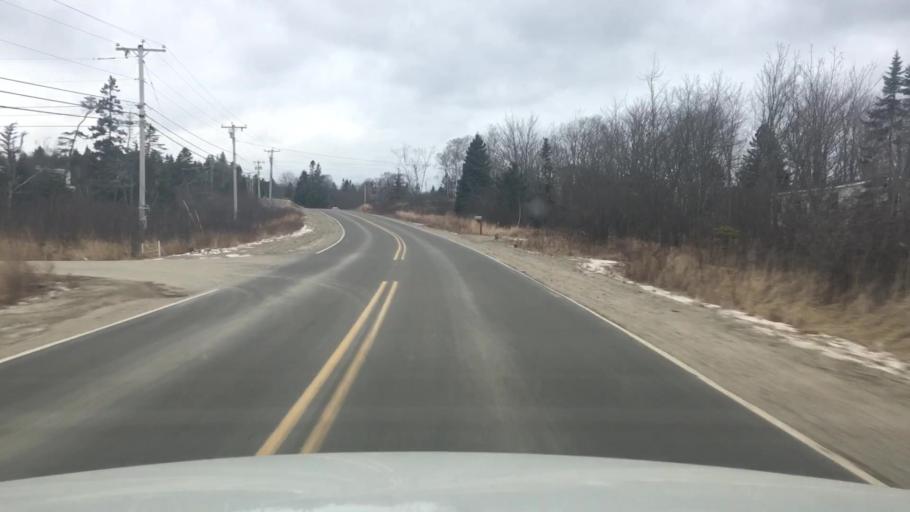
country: US
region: Maine
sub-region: Washington County
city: Jonesport
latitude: 44.5576
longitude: -67.6276
